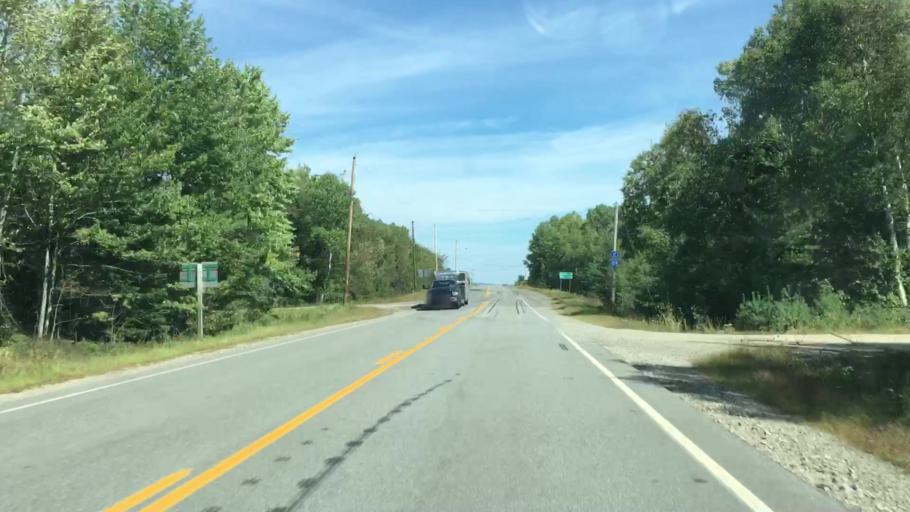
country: US
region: Maine
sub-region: Penobscot County
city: Howland
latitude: 45.2348
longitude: -68.6833
